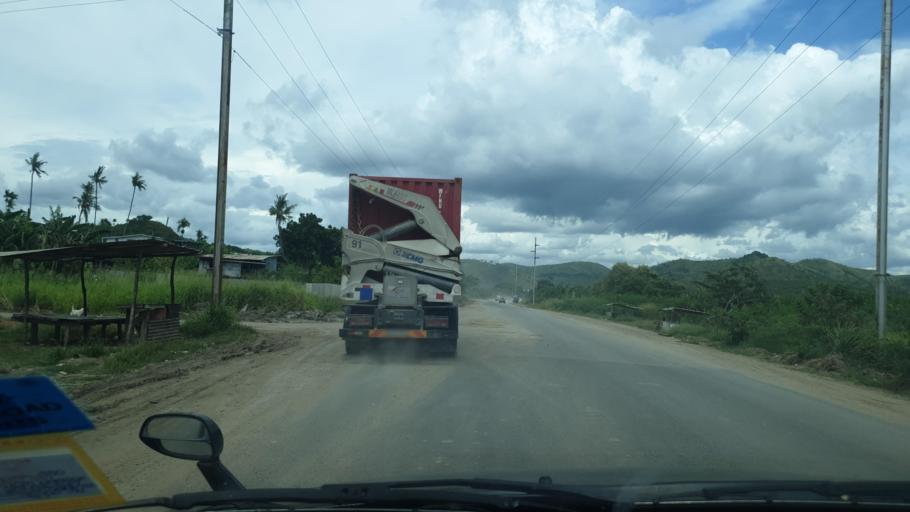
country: PG
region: National Capital
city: Port Moresby
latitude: -9.4176
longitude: 147.1216
